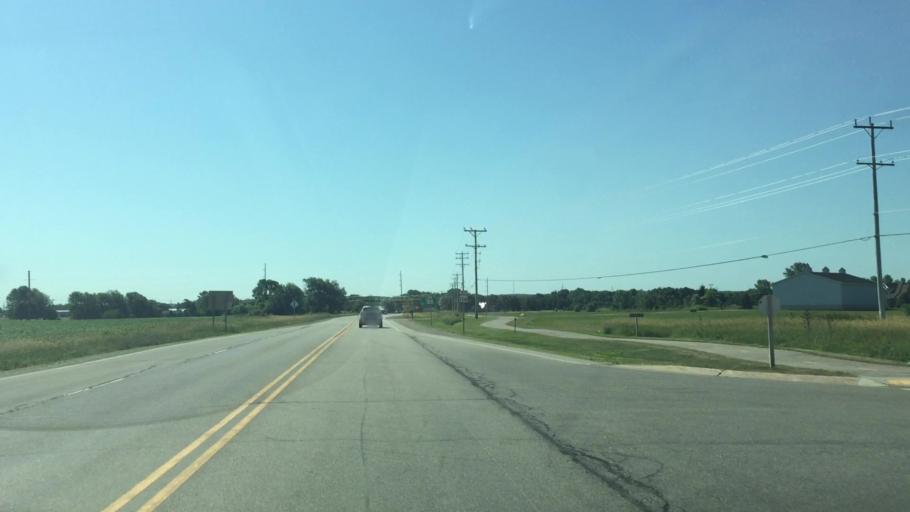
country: US
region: Wisconsin
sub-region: Outagamie County
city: Combined Locks
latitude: 44.2037
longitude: -88.3288
